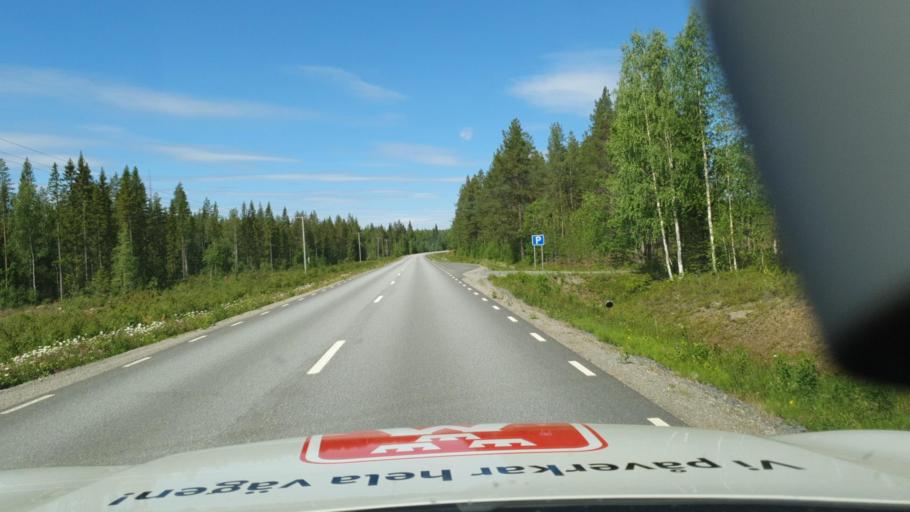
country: SE
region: Vaesterbotten
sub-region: Skelleftea Kommun
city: Boliden
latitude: 64.7451
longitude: 20.3562
